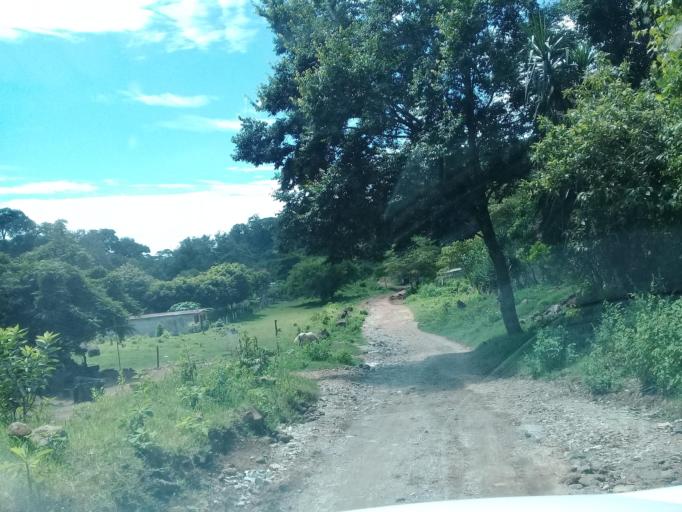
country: MX
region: Veracruz
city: El Castillo
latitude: 19.5704
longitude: -96.8865
